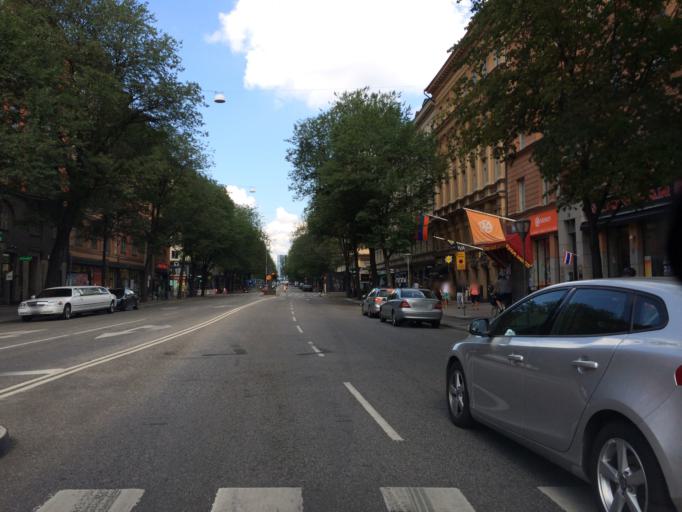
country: SE
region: Stockholm
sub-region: Stockholms Kommun
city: Stockholm
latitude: 59.3396
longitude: 18.0598
